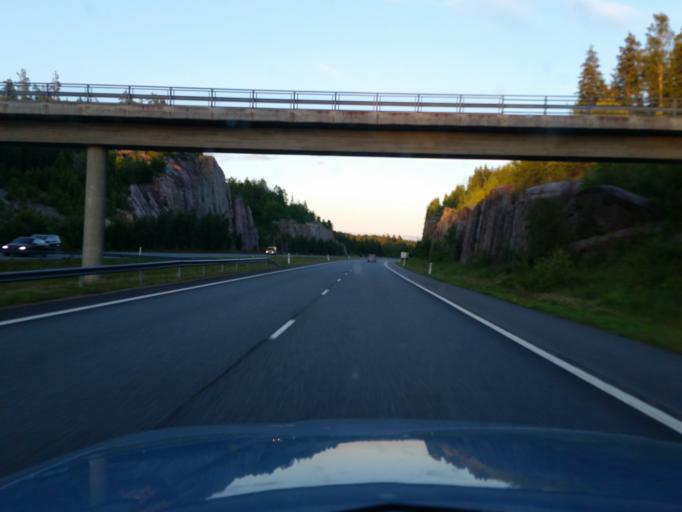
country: FI
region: Varsinais-Suomi
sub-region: Salo
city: Pertteli
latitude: 60.3988
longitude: 23.2433
